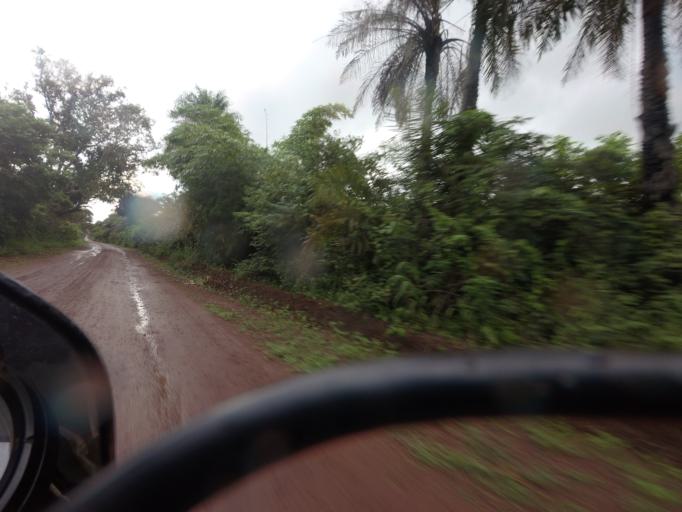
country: SL
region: Northern Province
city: Kukuna
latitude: 9.2533
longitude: -12.7812
